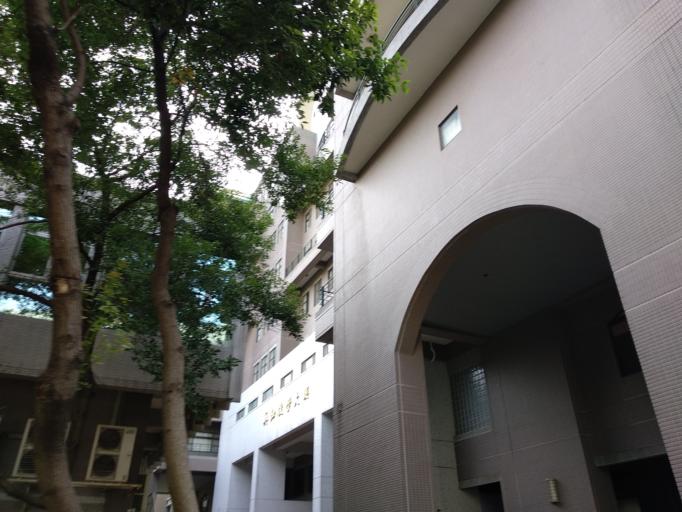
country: TW
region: Taiwan
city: Taoyuan City
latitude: 24.9566
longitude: 121.2415
